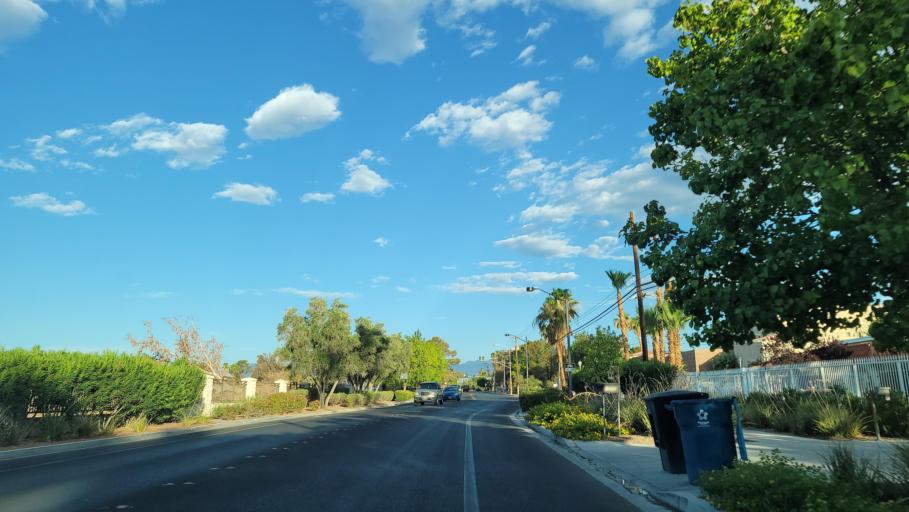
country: US
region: Nevada
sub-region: Clark County
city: Las Vegas
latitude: 36.1663
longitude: -115.1803
